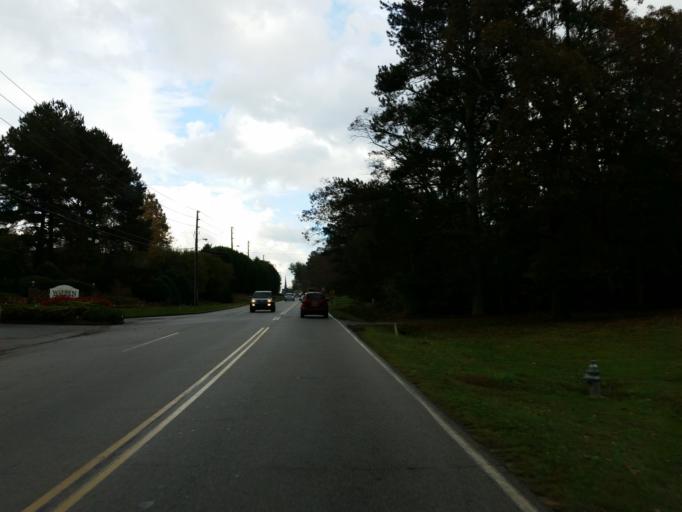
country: US
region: Georgia
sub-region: Henry County
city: Stockbridge
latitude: 33.4843
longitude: -84.2333
